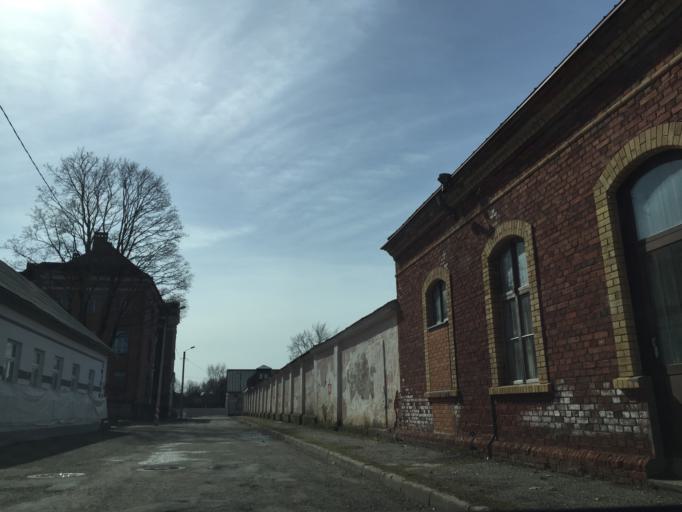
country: EE
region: Paernumaa
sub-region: Paernu linn
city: Parnu
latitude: 58.3855
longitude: 24.5200
